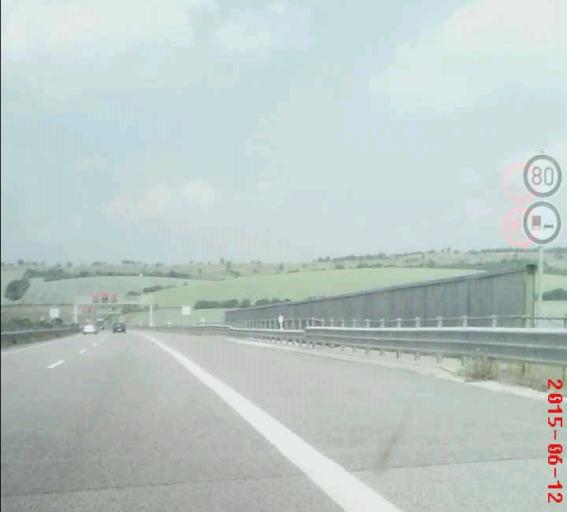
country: DE
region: Thuringia
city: Hemleben
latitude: 51.2625
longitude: 11.2085
